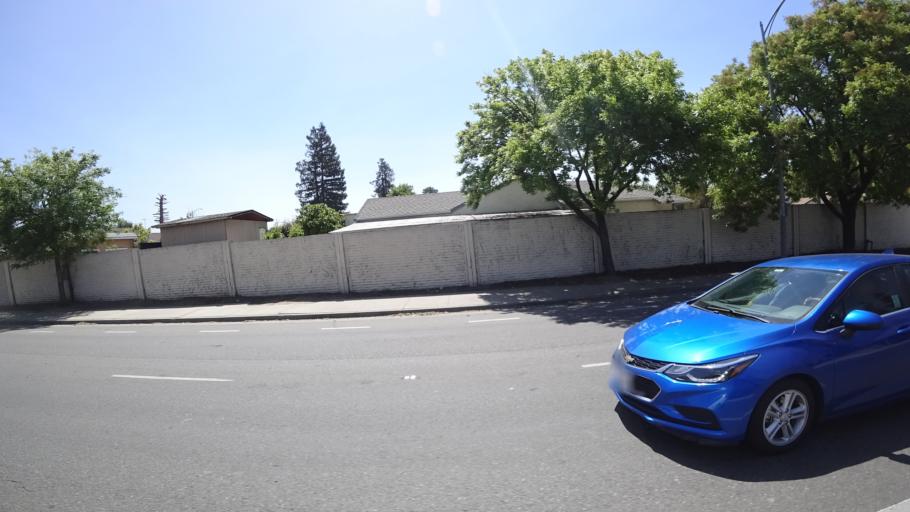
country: US
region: California
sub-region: Santa Clara County
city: Seven Trees
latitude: 37.3093
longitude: -121.8455
